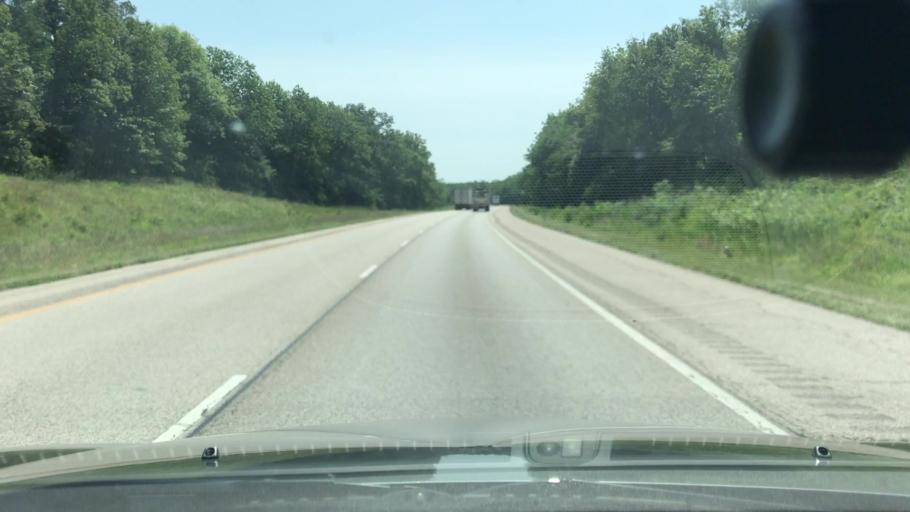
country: US
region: Illinois
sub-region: Washington County
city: Nashville
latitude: 38.3975
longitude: -89.3918
